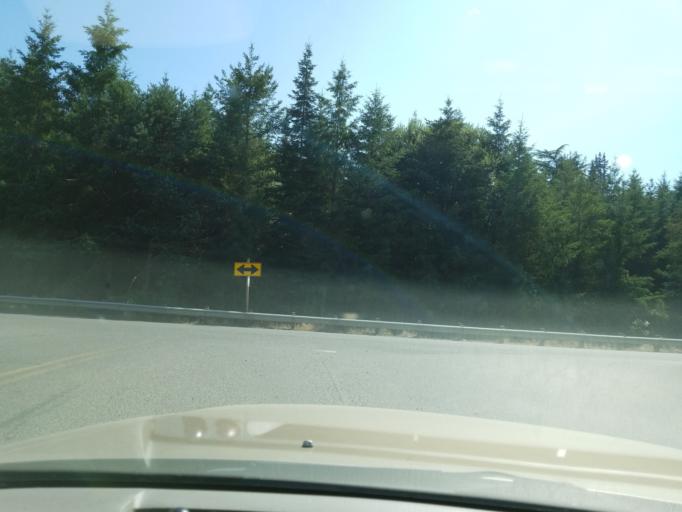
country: US
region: Oregon
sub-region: Yamhill County
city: McMinnville
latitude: 45.2303
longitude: -123.2320
